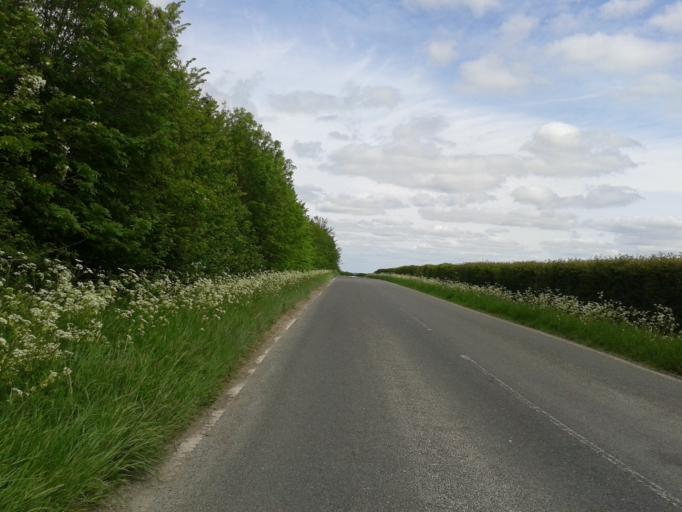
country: GB
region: England
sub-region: Cambridgeshire
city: Haslingfield
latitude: 52.1432
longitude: 0.0463
